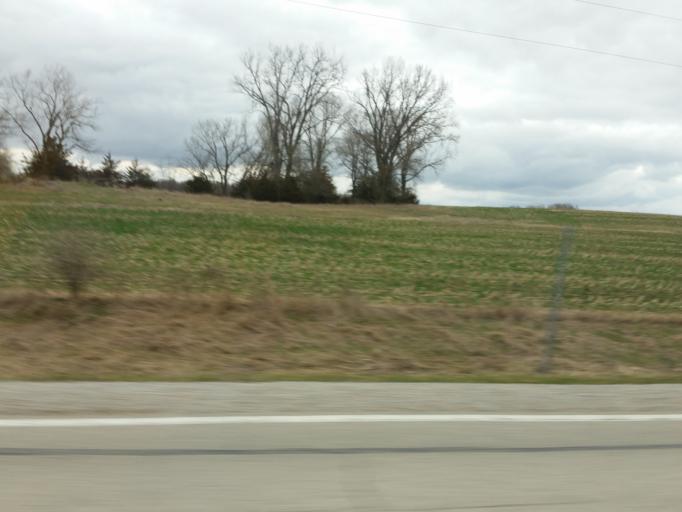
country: US
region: Iowa
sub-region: Benton County
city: Urbana
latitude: 42.3128
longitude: -91.9868
